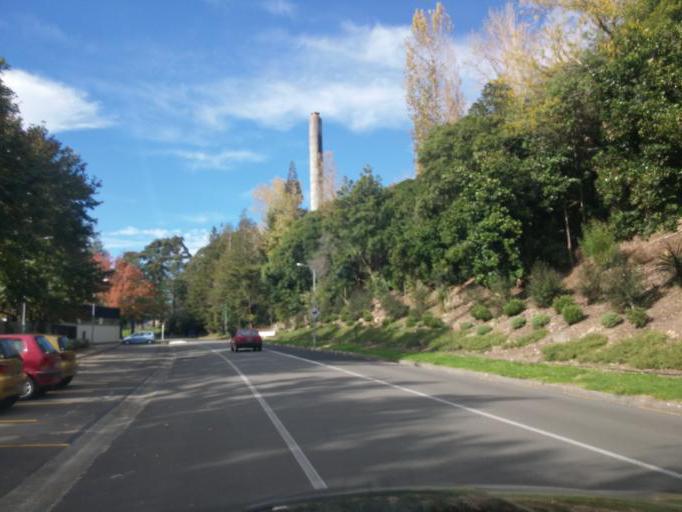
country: NZ
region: Manawatu-Wanganui
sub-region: Palmerston North City
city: Palmerston North
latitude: -40.3876
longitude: 175.6158
